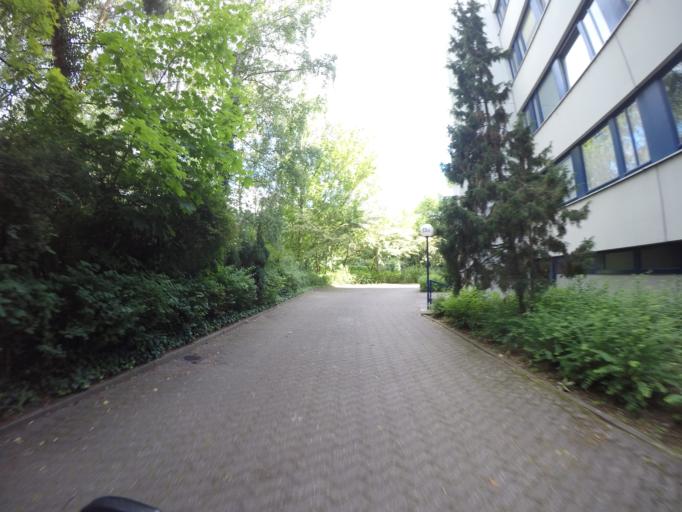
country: DE
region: Berlin
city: Zehlendorf Bezirk
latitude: 52.4324
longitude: 13.2719
